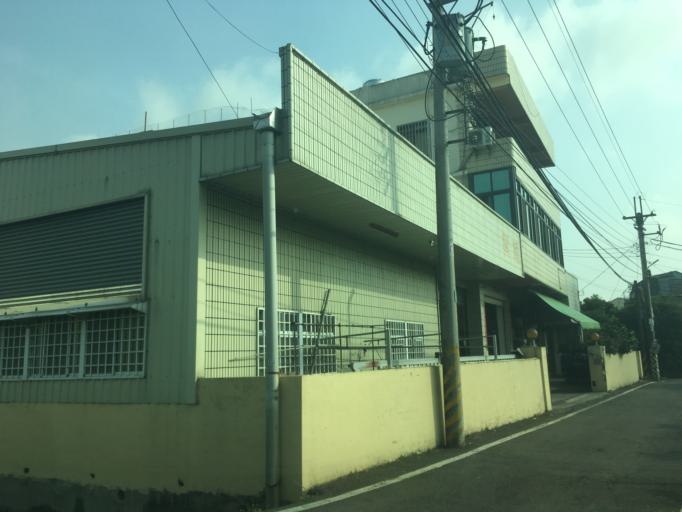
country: TW
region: Taiwan
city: Fengyuan
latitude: 24.2330
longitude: 120.7288
